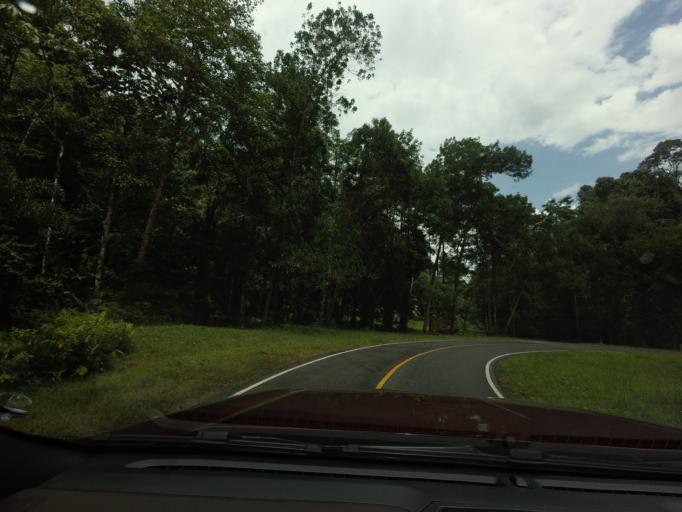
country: TH
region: Narathiwat
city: Sukhirin
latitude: 5.9294
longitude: 101.6504
